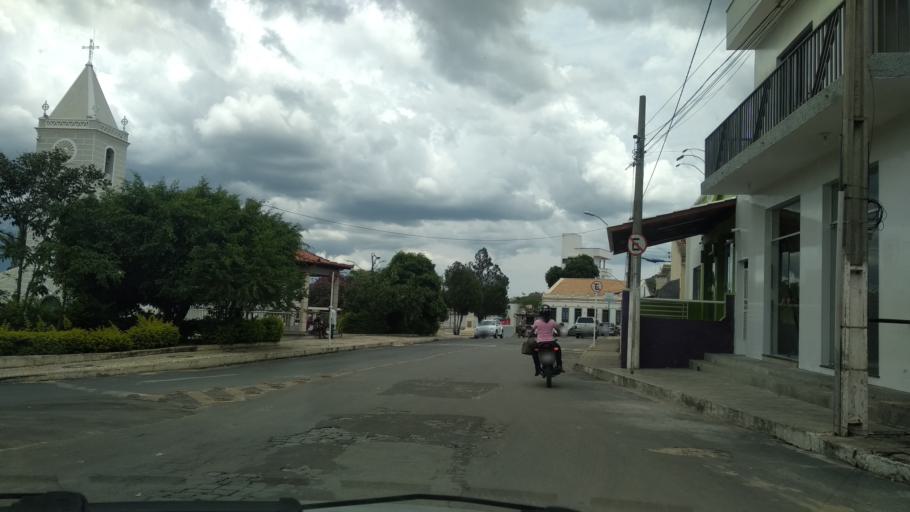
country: BR
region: Bahia
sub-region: Caetite
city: Caetite
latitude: -14.0694
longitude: -42.4857
